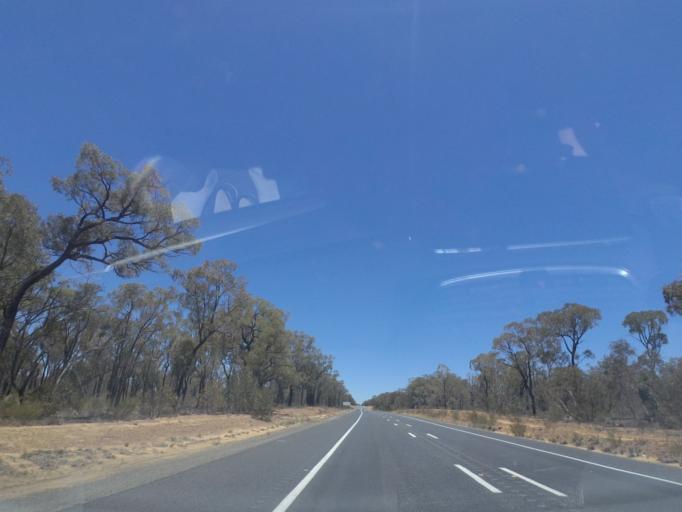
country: AU
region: New South Wales
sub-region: Warrumbungle Shire
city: Coonabarabran
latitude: -30.8896
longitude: 149.4429
